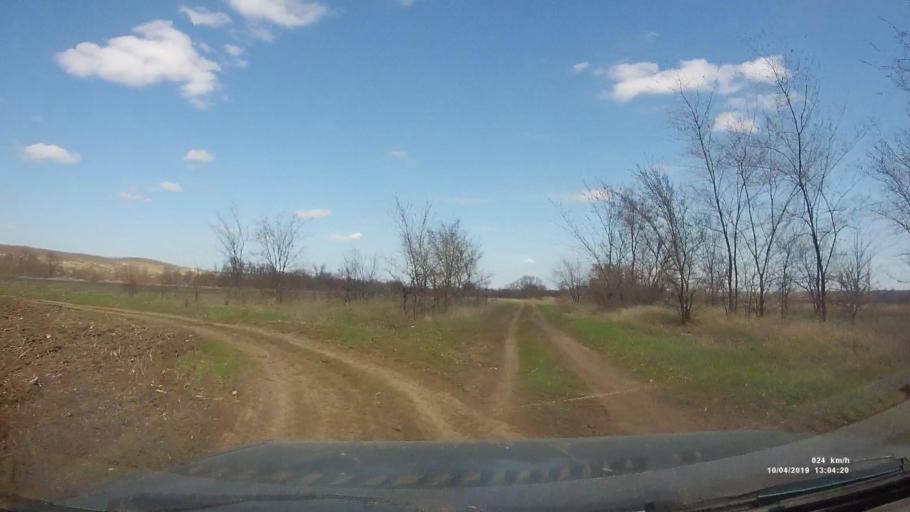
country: RU
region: Rostov
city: Masalovka
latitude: 48.3852
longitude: 40.2364
